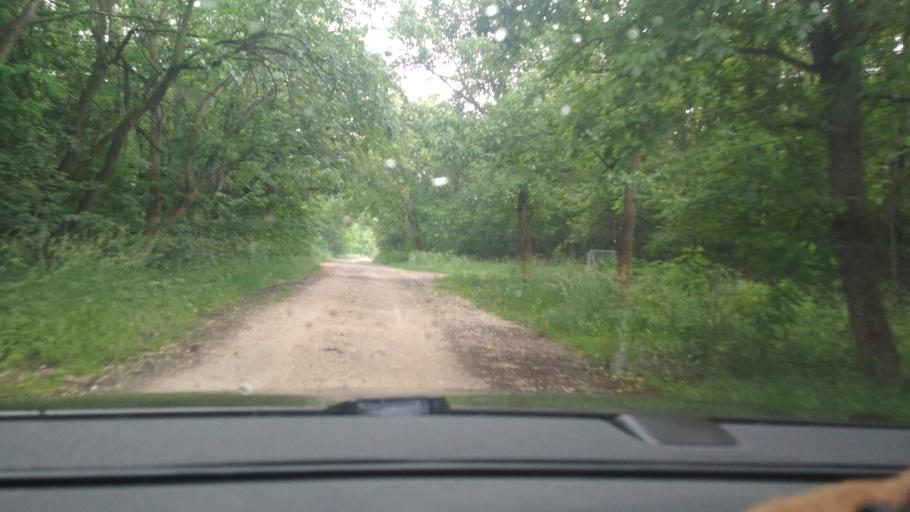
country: MD
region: Singerei
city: Biruinta
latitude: 47.7489
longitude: 28.1398
